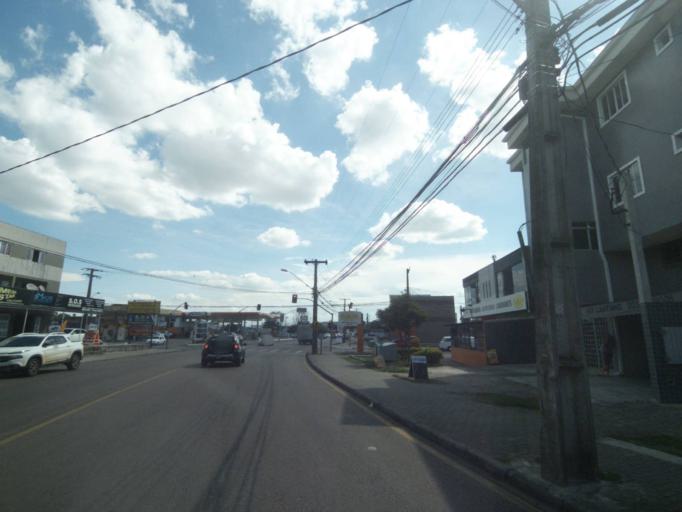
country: BR
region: Parana
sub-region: Pinhais
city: Pinhais
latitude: -25.4764
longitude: -49.2403
